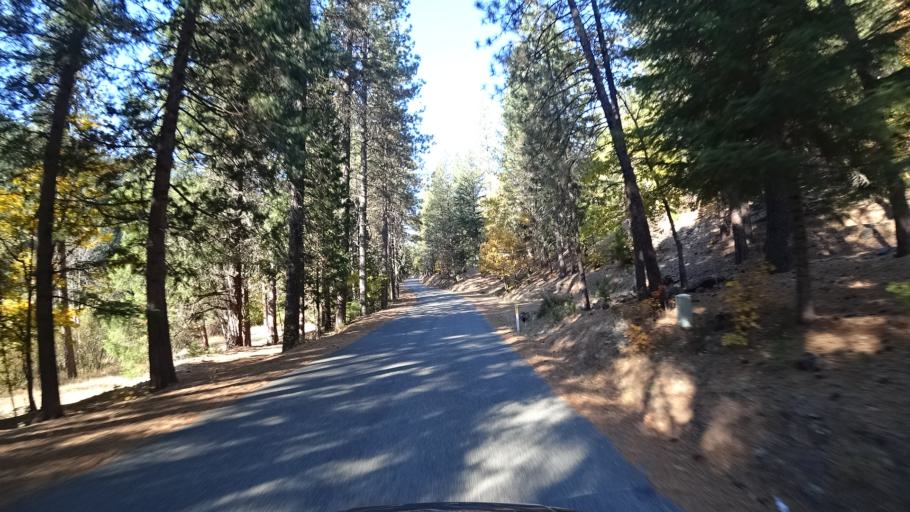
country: US
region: California
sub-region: Siskiyou County
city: Yreka
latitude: 41.6406
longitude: -123.0077
